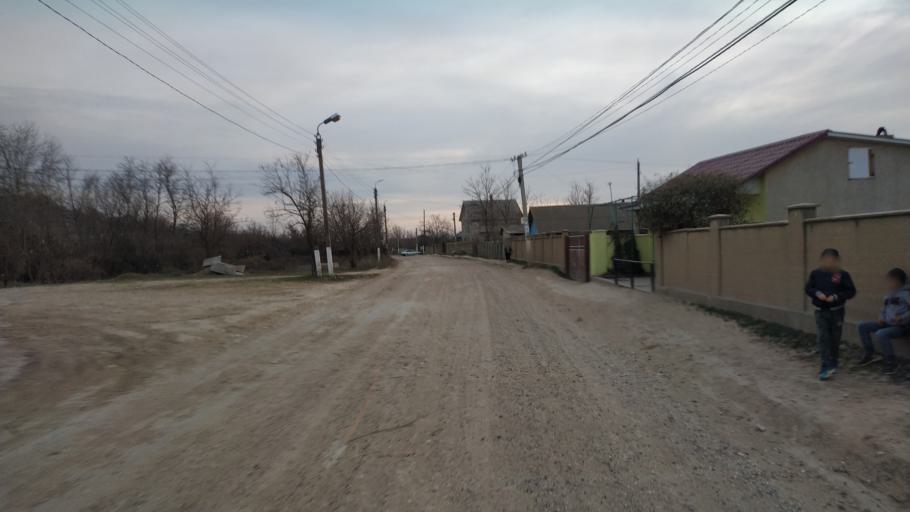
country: MD
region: Hincesti
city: Dancu
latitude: 46.7532
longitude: 28.2069
